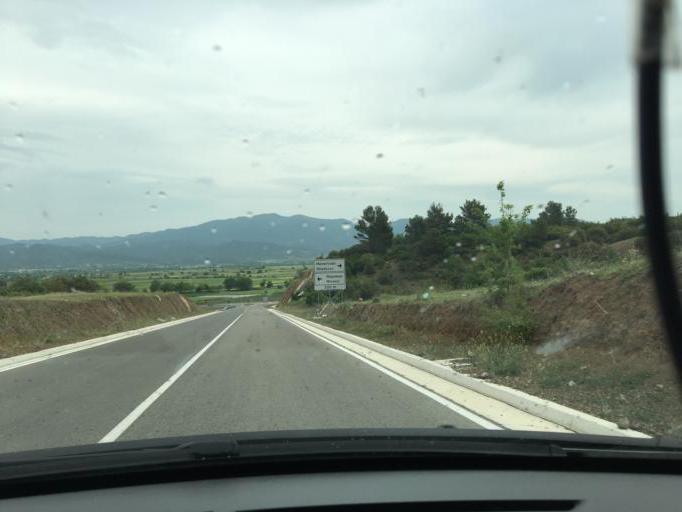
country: MK
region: Gevgelija
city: Miravci
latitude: 41.3019
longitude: 22.4417
